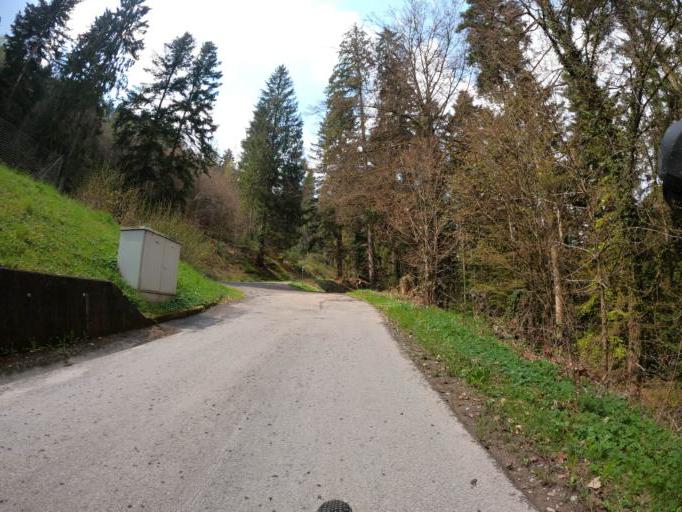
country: DE
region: Baden-Wuerttemberg
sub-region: Karlsruhe Region
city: Calw
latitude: 48.7369
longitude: 8.7195
